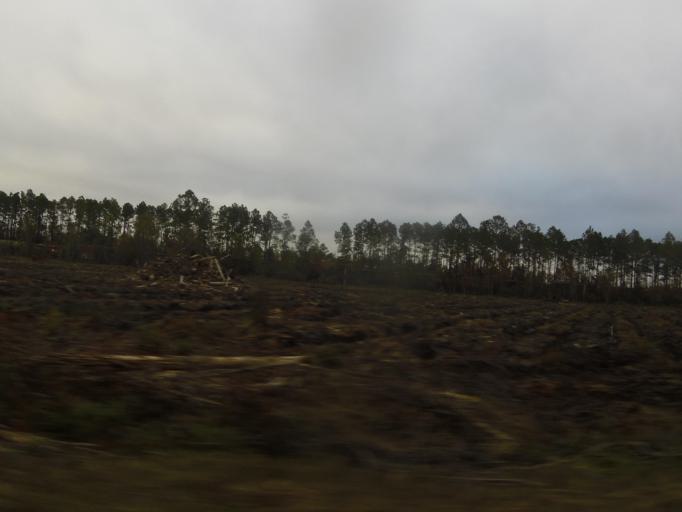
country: US
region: Georgia
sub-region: Charlton County
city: Folkston
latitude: 30.8661
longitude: -82.0390
